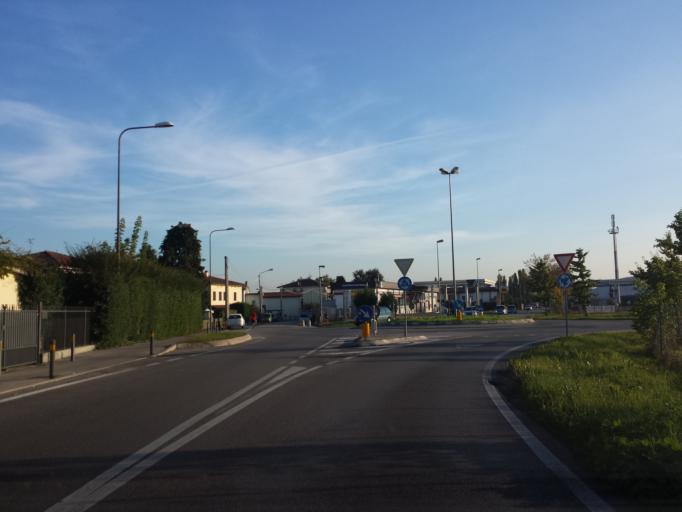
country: IT
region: Veneto
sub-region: Provincia di Vicenza
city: Vicenza
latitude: 45.5757
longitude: 11.5361
